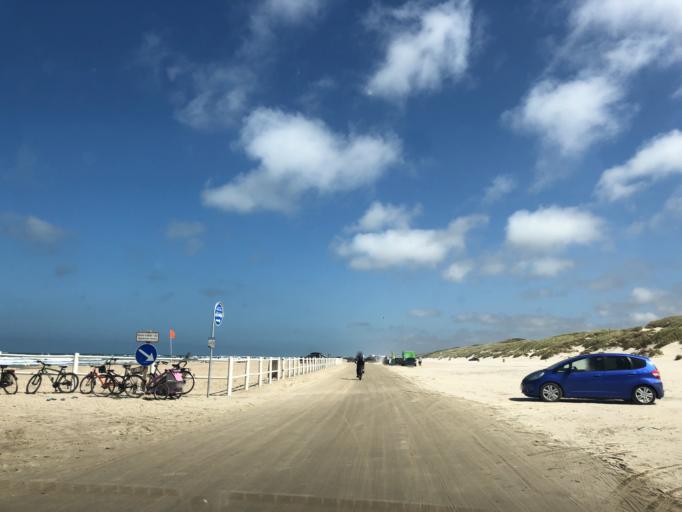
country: DK
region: North Denmark
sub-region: Jammerbugt Kommune
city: Pandrup
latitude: 57.2564
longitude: 9.5809
